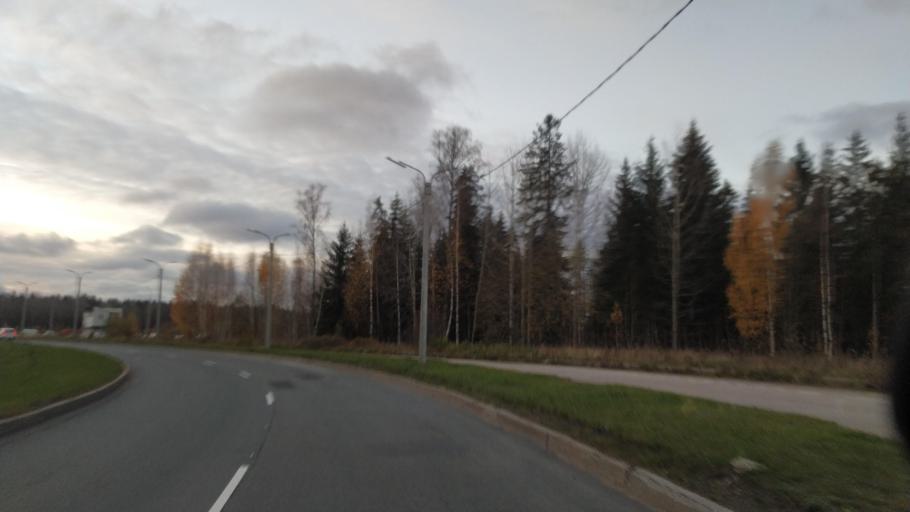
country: RU
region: Leningrad
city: Sosnovyy Bor
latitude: 59.9179
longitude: 29.0905
